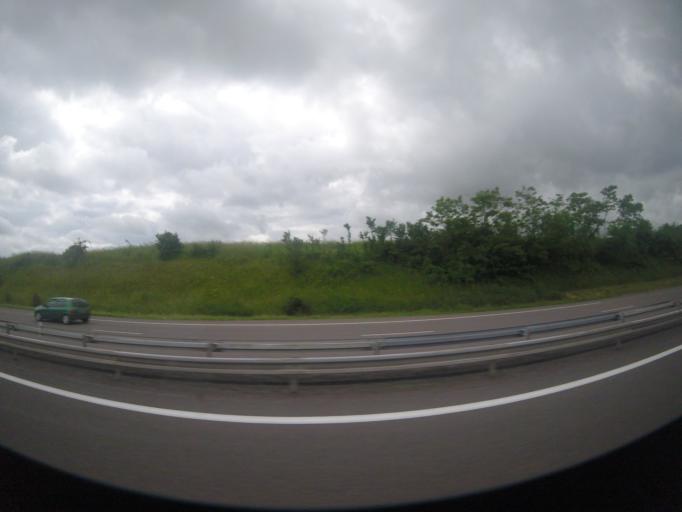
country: FR
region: Lorraine
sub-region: Departement de Meurthe-et-Moselle
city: Valleroy
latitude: 49.2040
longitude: 5.9569
